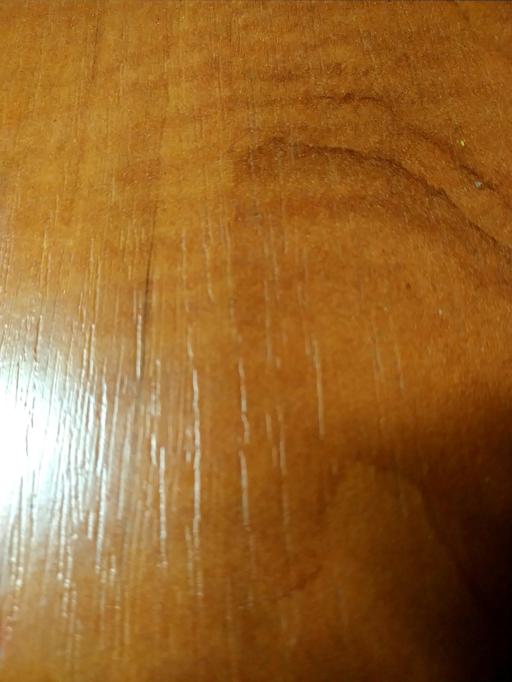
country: RU
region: Smolensk
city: Yartsevo
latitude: 55.4347
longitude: 32.7959
